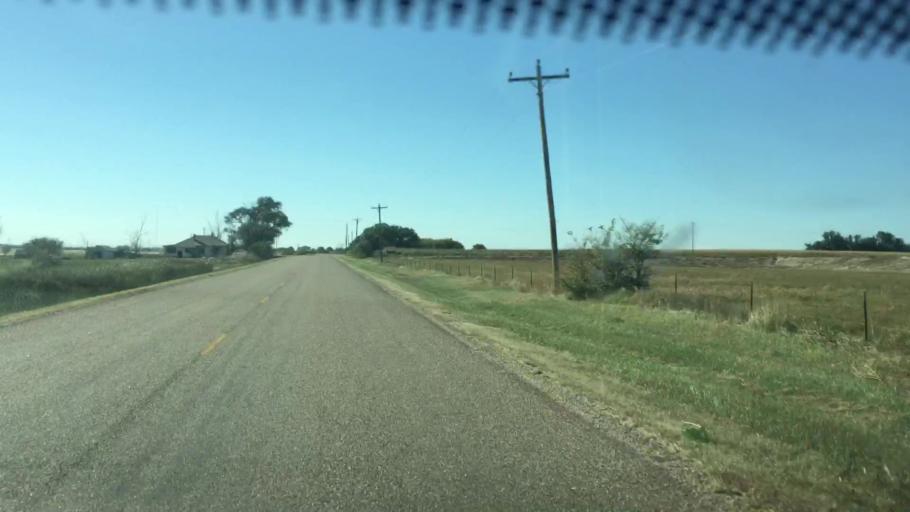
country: US
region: Colorado
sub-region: Prowers County
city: Lamar
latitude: 38.1157
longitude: -102.5914
